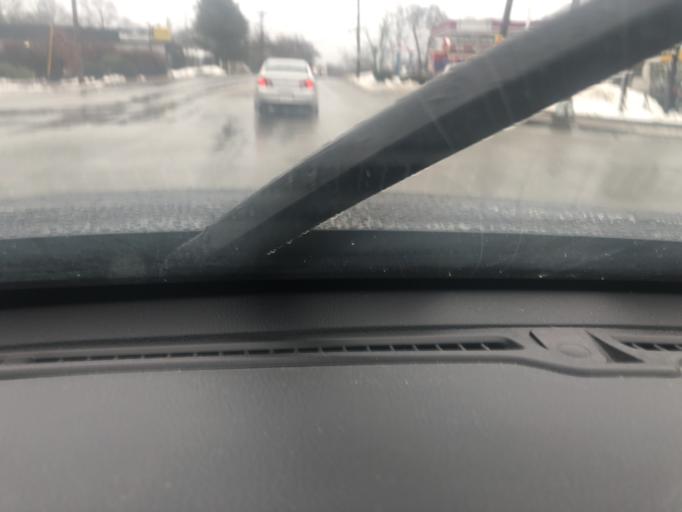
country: US
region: Massachusetts
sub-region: Norfolk County
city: Avon
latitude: 42.1017
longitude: -71.0529
